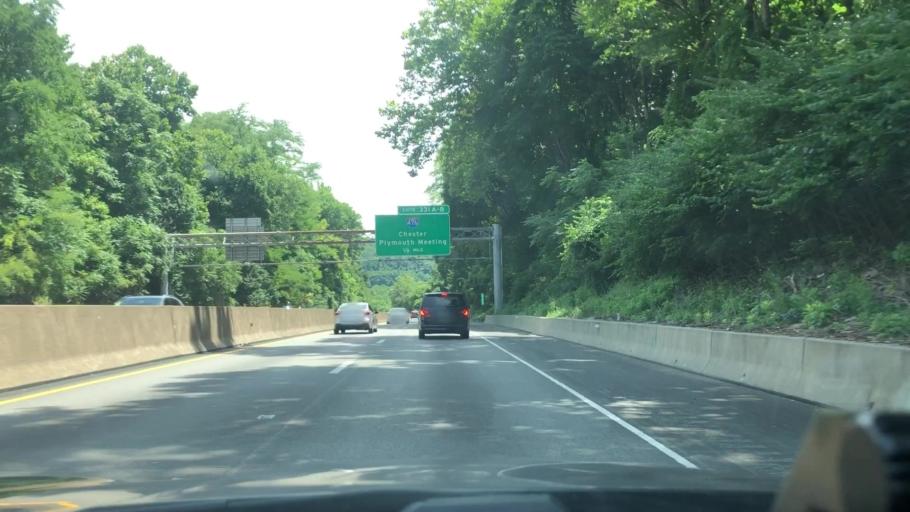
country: US
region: Pennsylvania
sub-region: Montgomery County
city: West Conshohocken
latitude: 40.0661
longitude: -75.3332
